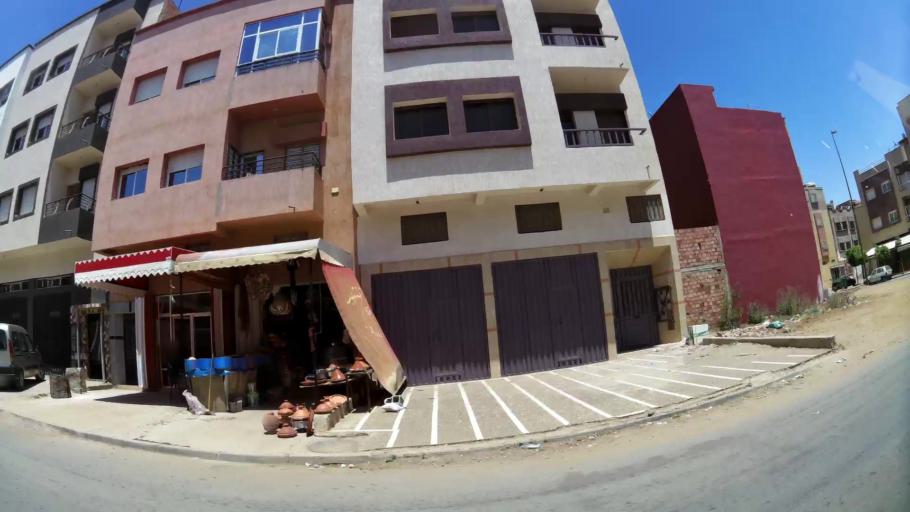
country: MA
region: Gharb-Chrarda-Beni Hssen
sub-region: Kenitra Province
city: Kenitra
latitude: 34.2315
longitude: -6.6128
